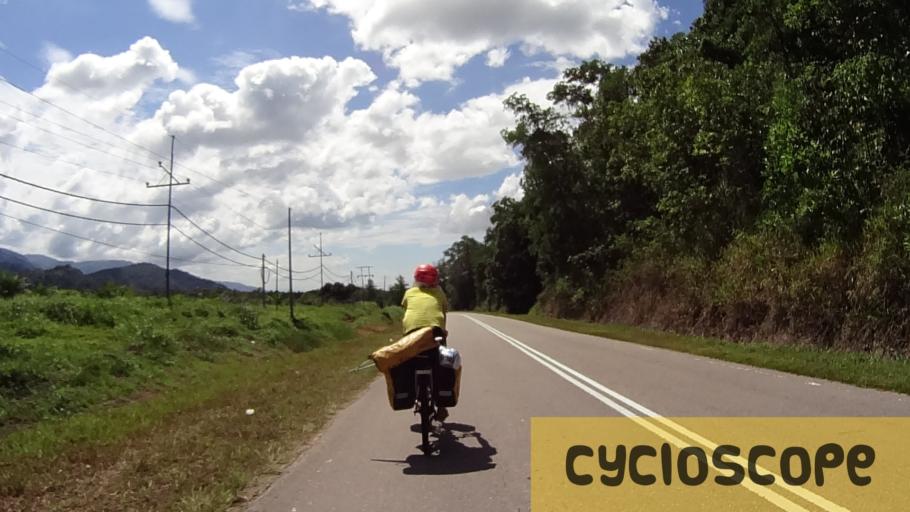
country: MY
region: Sabah
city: Beaufort
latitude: 5.1364
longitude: 115.6434
